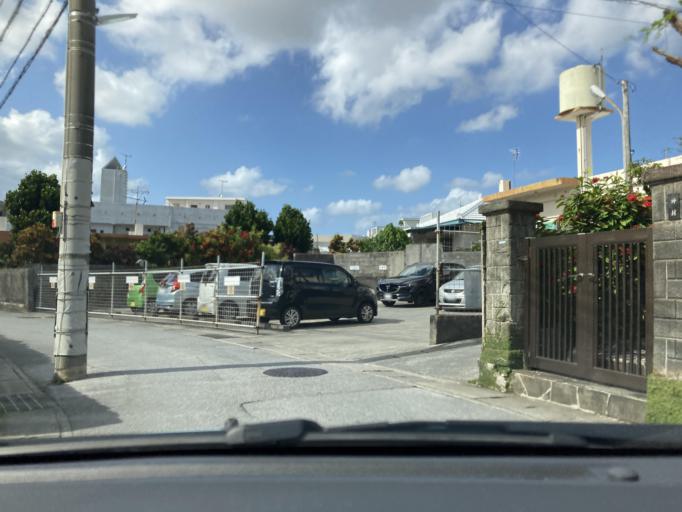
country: JP
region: Okinawa
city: Naha-shi
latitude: 26.2107
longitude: 127.7132
